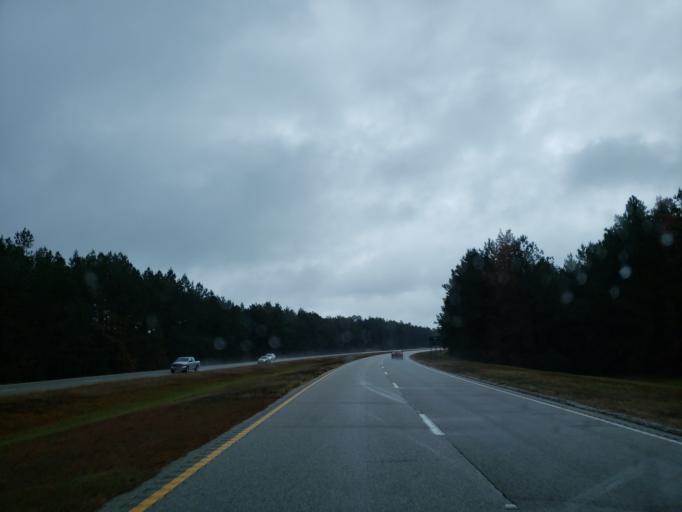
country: US
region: Mississippi
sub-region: Lauderdale County
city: Meridian
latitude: 32.2829
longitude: -88.6979
